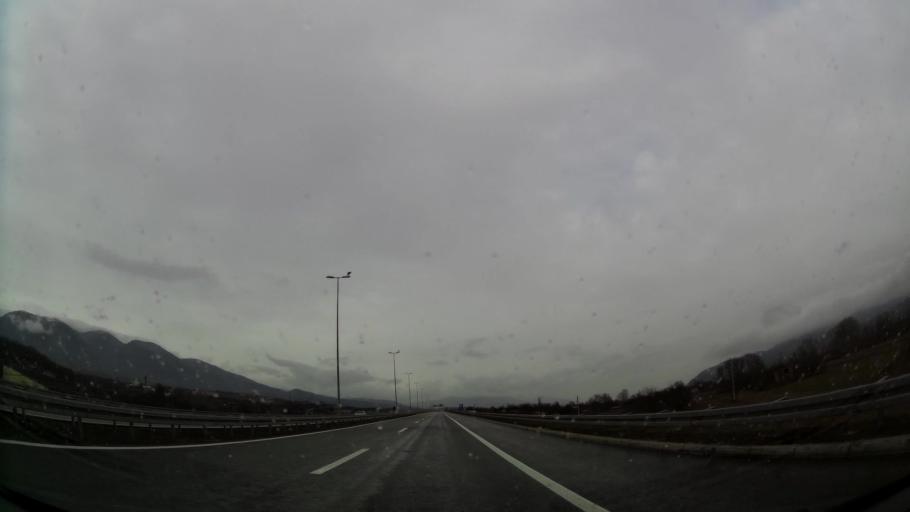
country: RS
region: Central Serbia
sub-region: Pcinjski Okrug
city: Vranje
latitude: 42.5395
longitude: 21.9280
